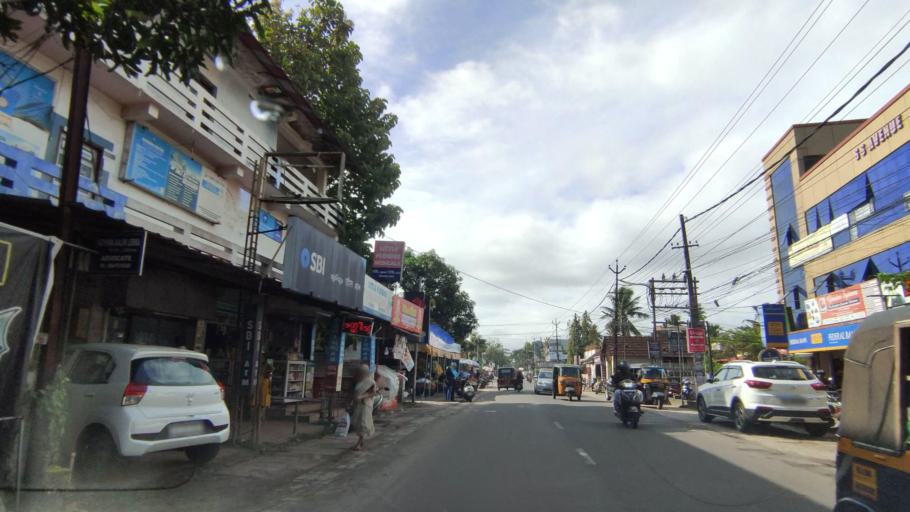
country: IN
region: Kerala
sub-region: Alappuzha
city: Alleppey
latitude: 9.5074
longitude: 76.3400
